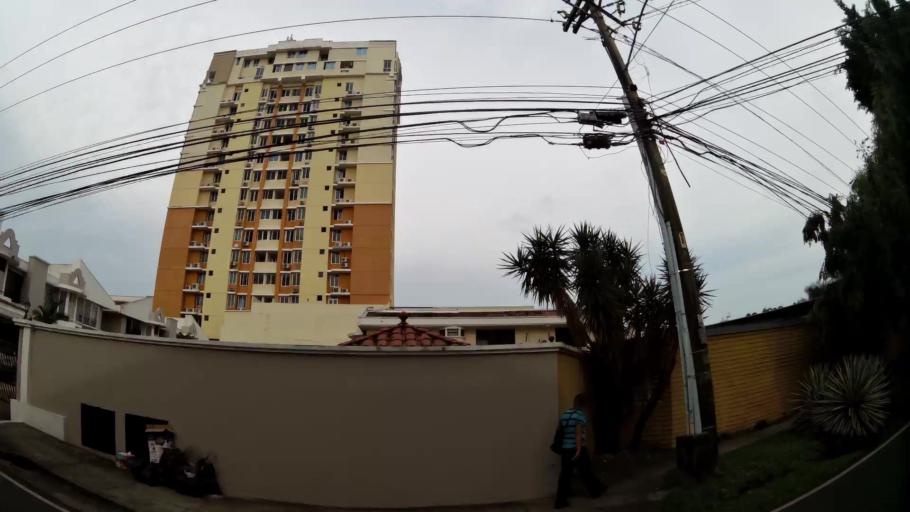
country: PA
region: Panama
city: Panama
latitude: 9.0040
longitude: -79.5056
